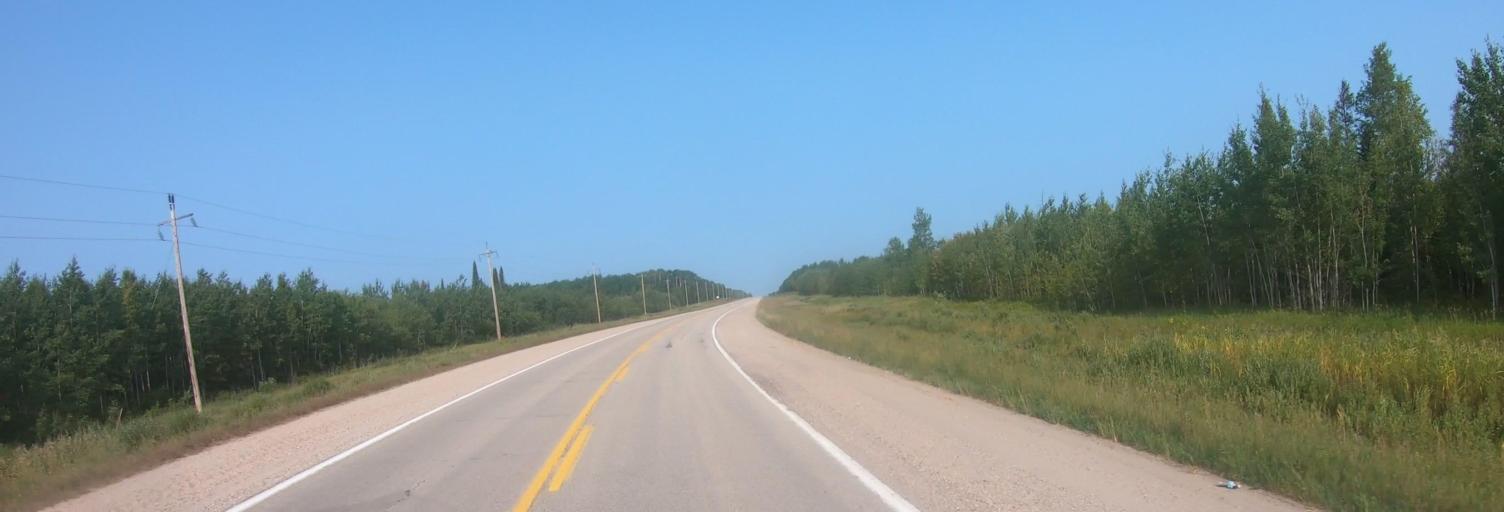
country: US
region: Minnesota
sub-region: Roseau County
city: Roseau
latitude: 49.0239
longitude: -95.7384
